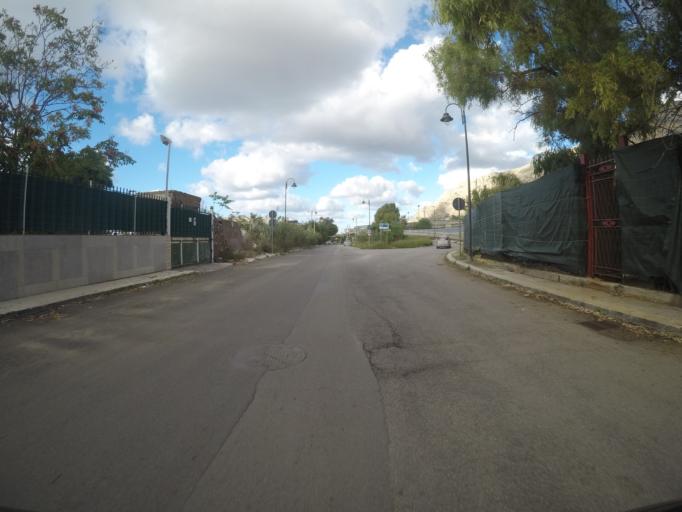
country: IT
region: Sicily
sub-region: Palermo
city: Isola delle Femmine
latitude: 38.1877
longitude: 13.2435
